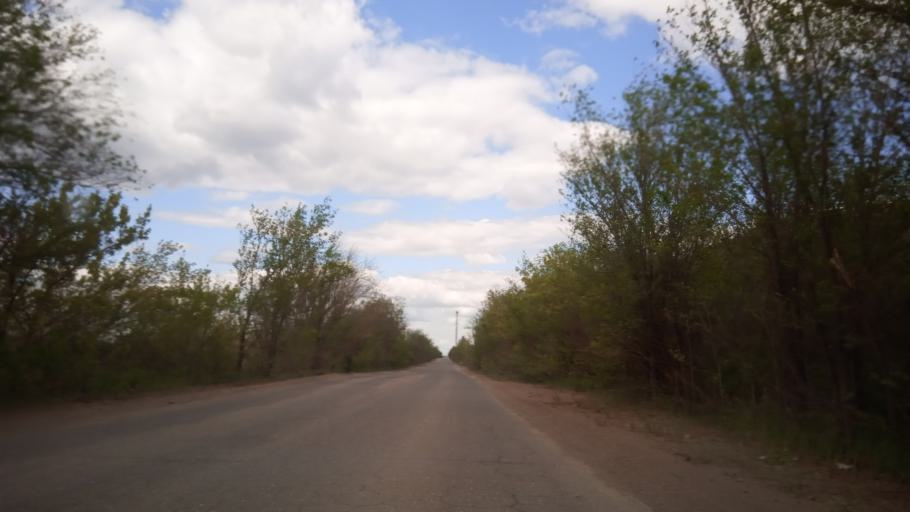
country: RU
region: Orenburg
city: Novotroitsk
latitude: 51.2446
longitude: 58.3587
